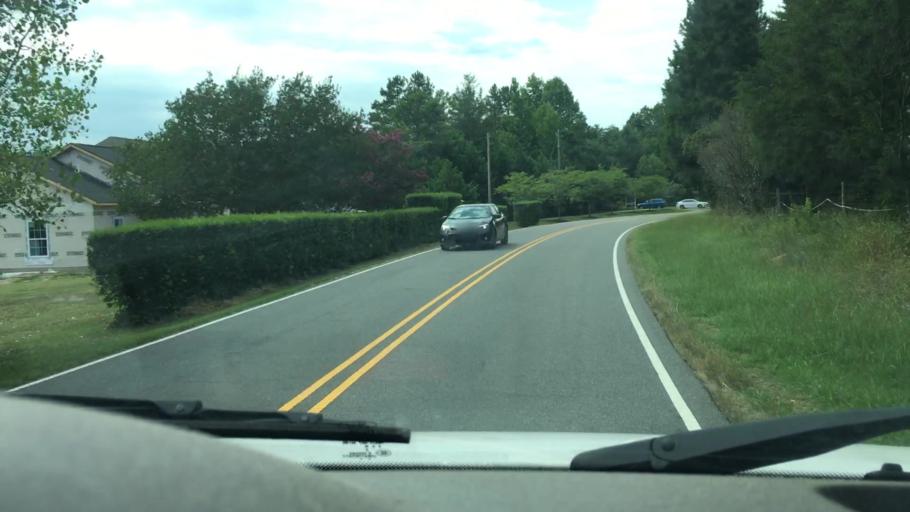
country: US
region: North Carolina
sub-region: Gaston County
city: Davidson
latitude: 35.4749
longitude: -80.8010
